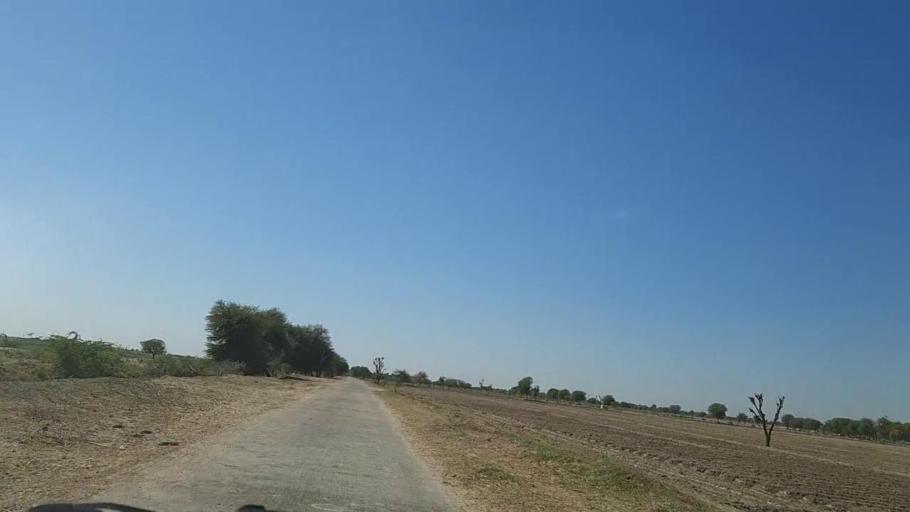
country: PK
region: Sindh
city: Dhoro Naro
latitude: 25.5227
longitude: 69.5223
